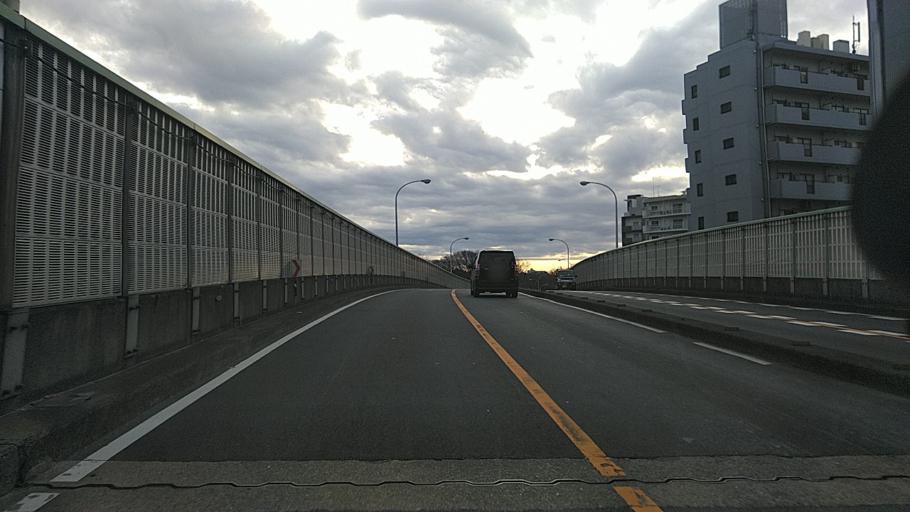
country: JP
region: Saitama
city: Yashio-shi
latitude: 35.7762
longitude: 139.8428
